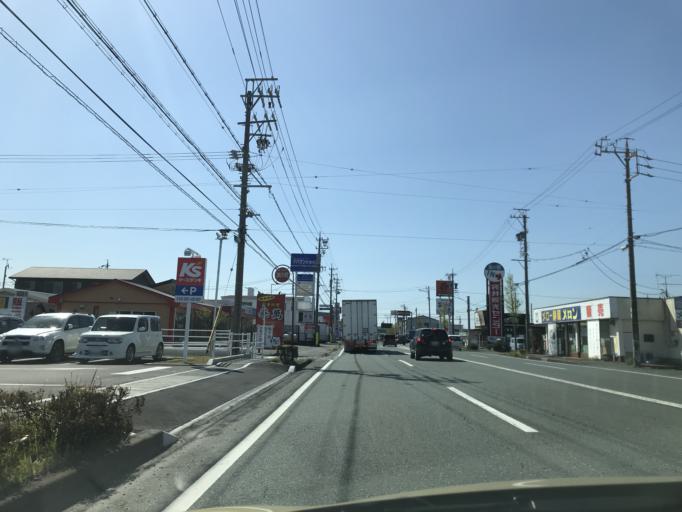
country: JP
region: Shizuoka
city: Fukuroi
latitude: 34.7567
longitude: 137.9065
